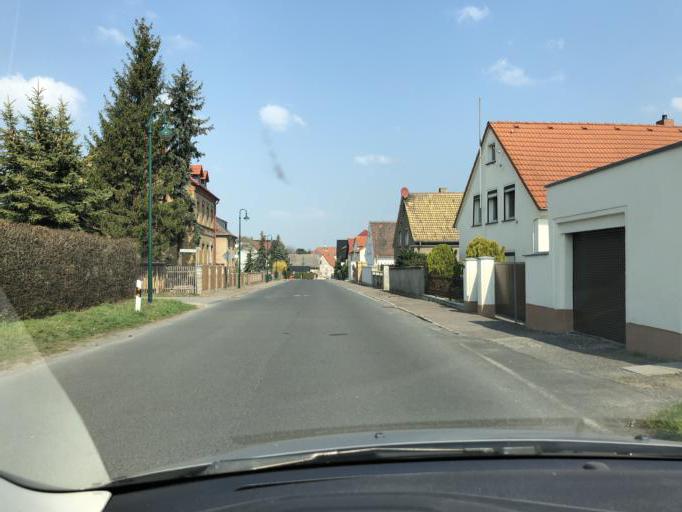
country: DE
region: Saxony
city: Rackwitz
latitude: 51.4237
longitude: 12.3814
